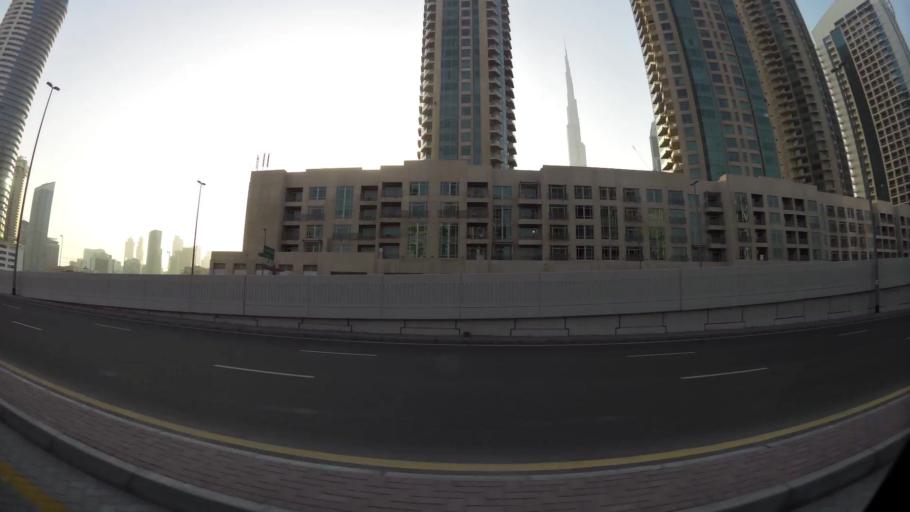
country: AE
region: Dubai
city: Dubai
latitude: 25.1894
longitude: 55.2820
